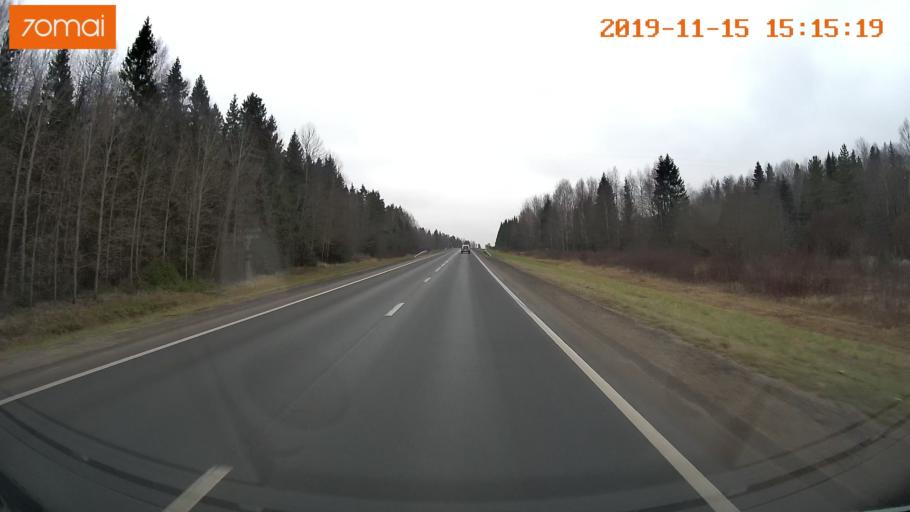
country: RU
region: Jaroslavl
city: Danilov
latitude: 58.2864
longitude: 40.1996
